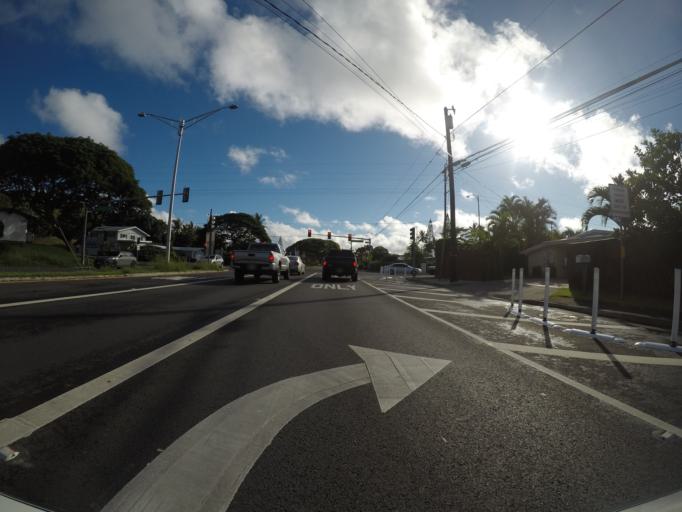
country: US
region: Hawaii
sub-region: Honolulu County
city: Kailua
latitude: 21.4093
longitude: -157.7552
